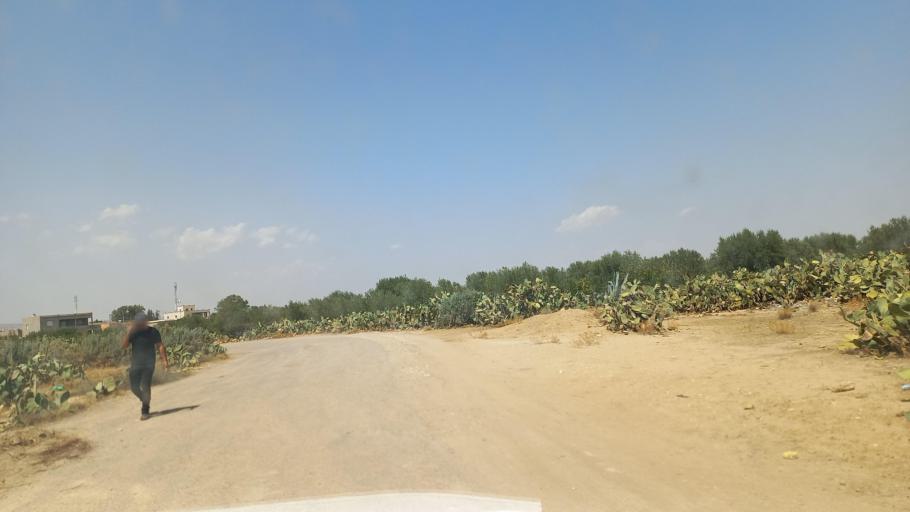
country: TN
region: Al Qasrayn
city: Kasserine
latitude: 35.2467
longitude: 9.0287
